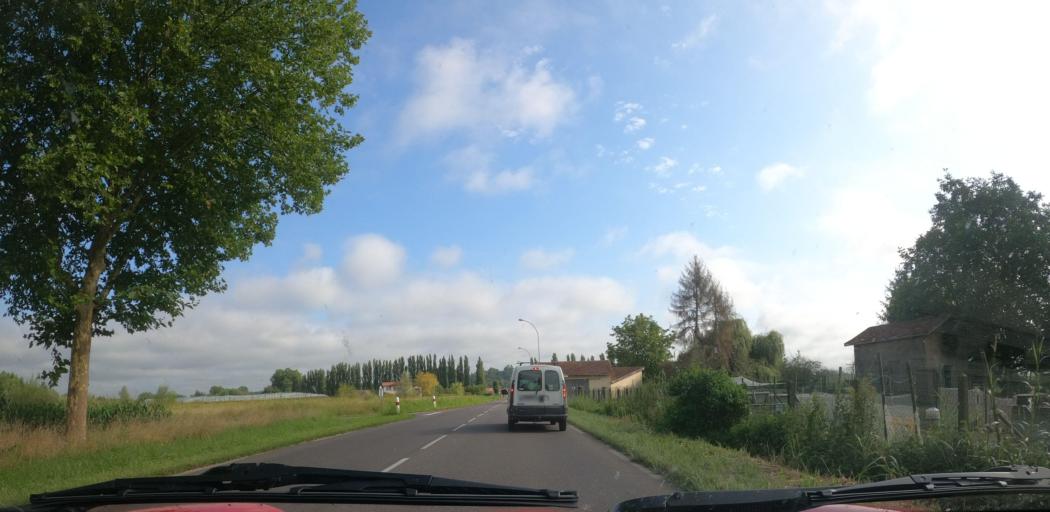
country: FR
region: Aquitaine
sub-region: Departement des Landes
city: Peyrehorade
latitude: 43.5364
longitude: -1.1085
